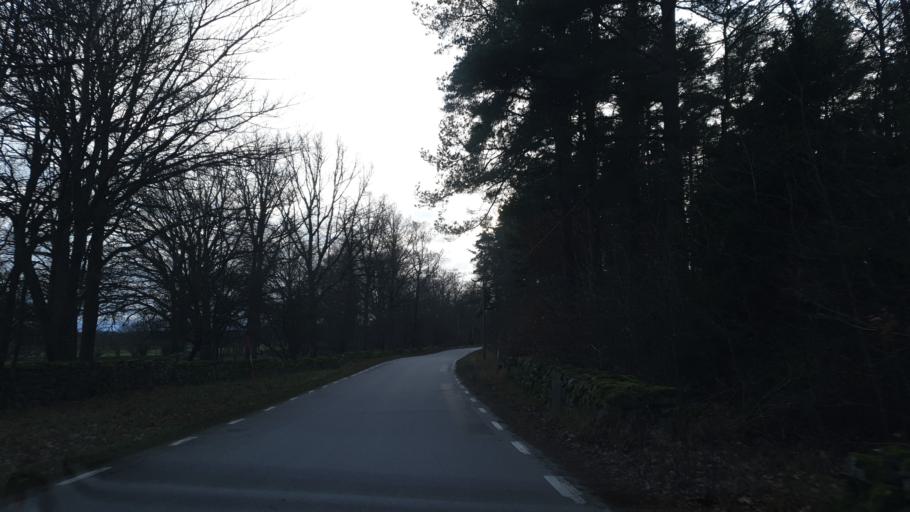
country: SE
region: Blekinge
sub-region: Karlskrona Kommun
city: Jaemjoe
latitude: 56.2028
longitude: 15.9573
